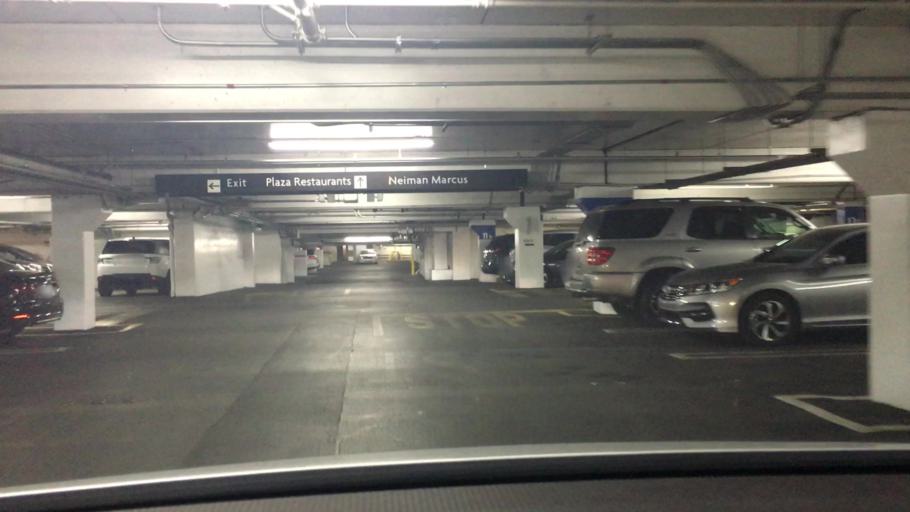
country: US
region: Nevada
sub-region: Clark County
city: Paradise
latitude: 36.1272
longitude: -115.1705
